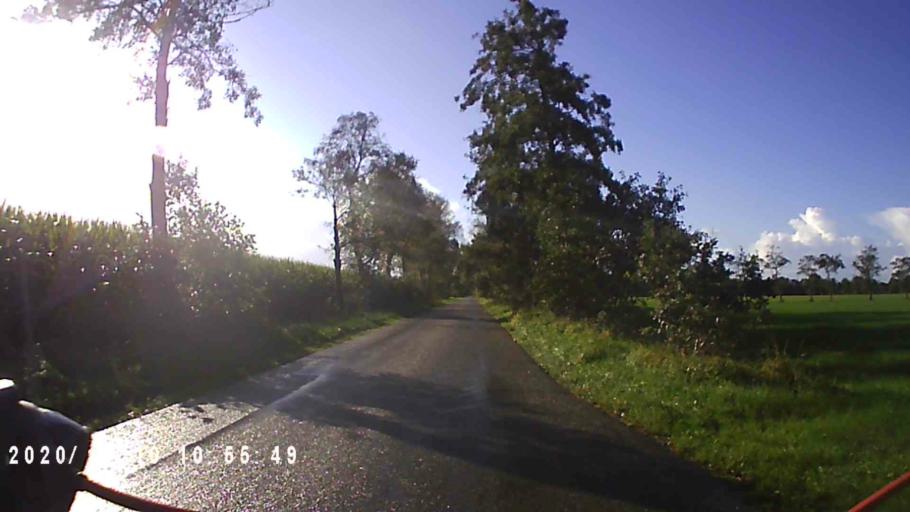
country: NL
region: Friesland
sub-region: Gemeente Achtkarspelen
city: Surhuisterveen
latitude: 53.1538
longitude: 6.2066
